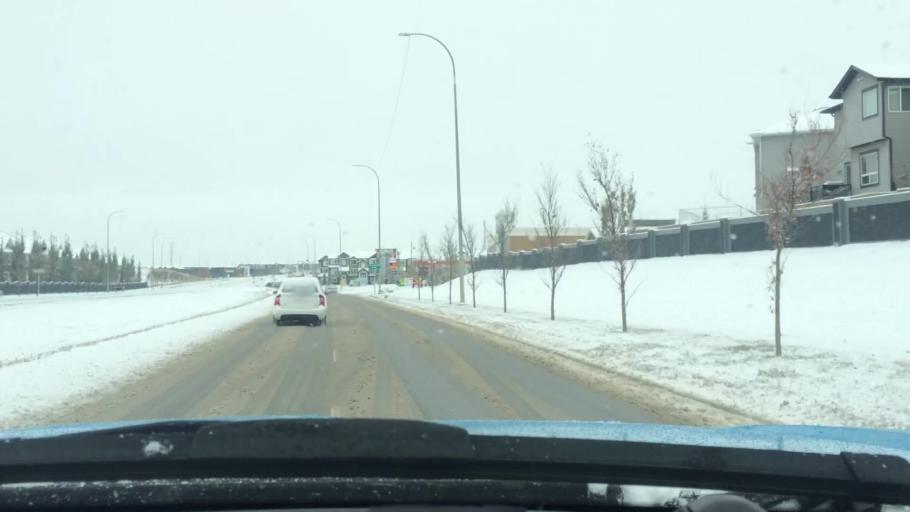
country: CA
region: Alberta
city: Calgary
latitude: 51.1748
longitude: -114.1567
